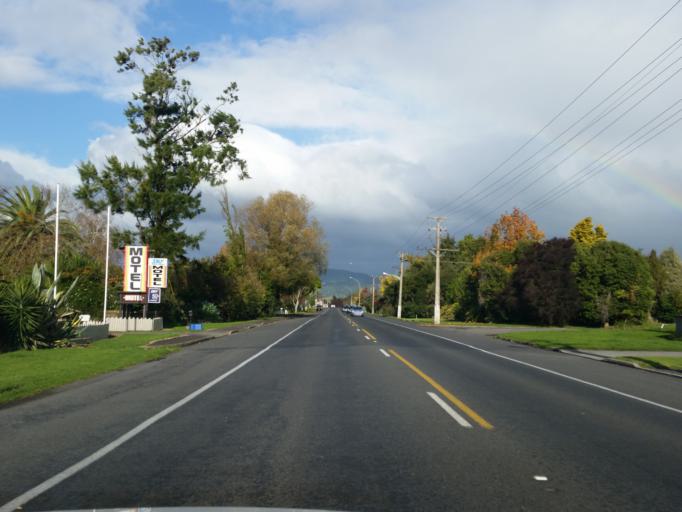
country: NZ
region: Waikato
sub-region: Hauraki District
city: Paeroa
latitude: -37.3684
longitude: 175.6607
